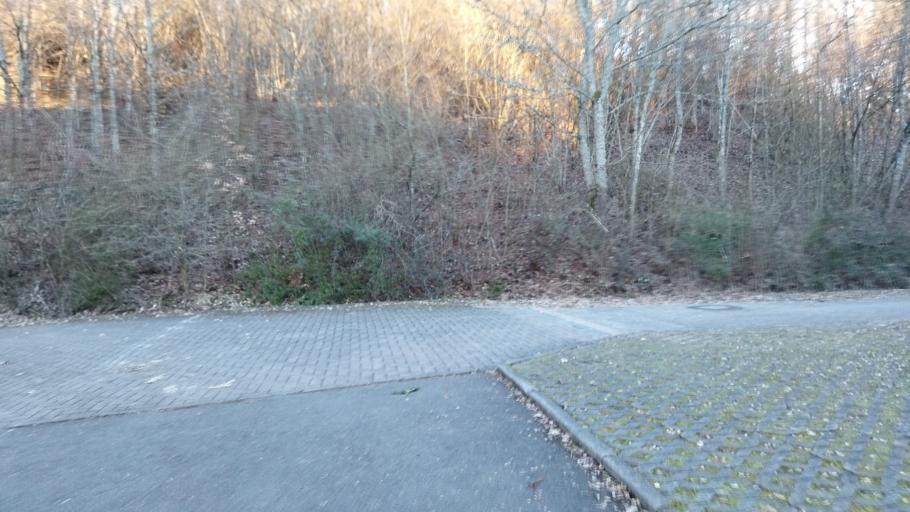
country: DE
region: Rheinland-Pfalz
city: Schonenberg-Kubelberg
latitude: 49.4129
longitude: 7.3663
